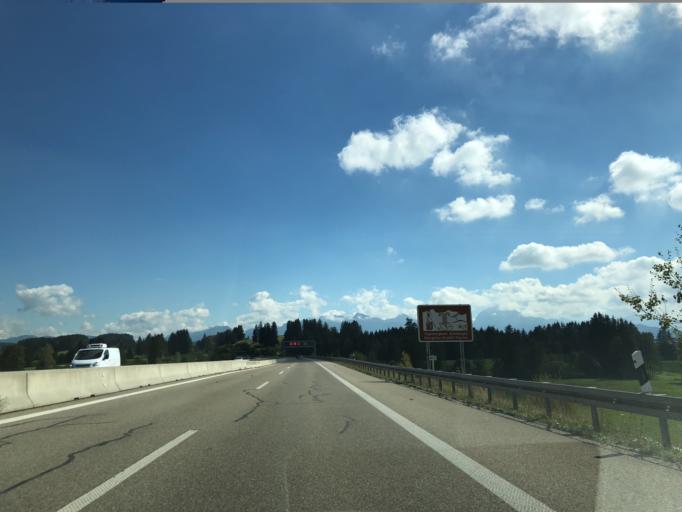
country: DE
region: Bavaria
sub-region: Swabia
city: Eisenberg
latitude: 47.6280
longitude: 10.6080
